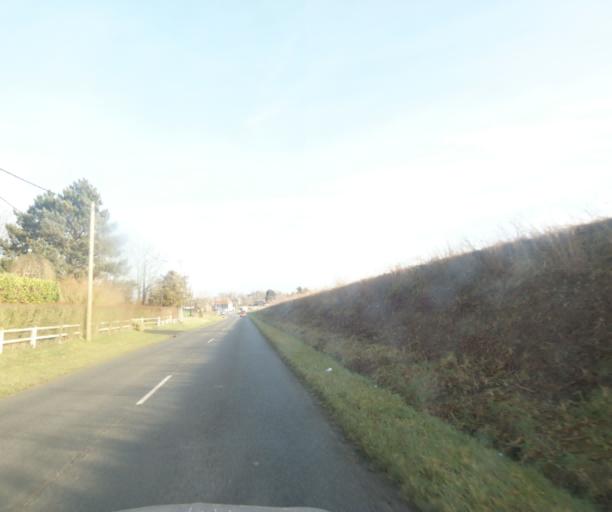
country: FR
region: Nord-Pas-de-Calais
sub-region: Departement du Nord
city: Thiant
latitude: 50.2836
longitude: 3.4463
